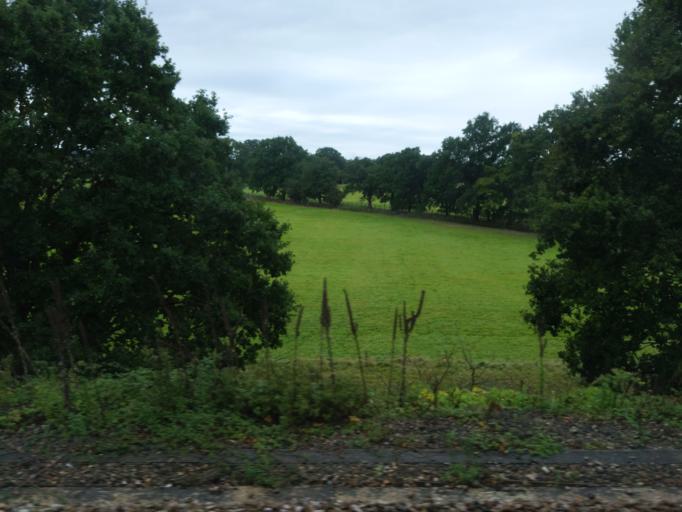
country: GB
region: England
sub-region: Kent
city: Tonbridge
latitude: 51.2059
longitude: 0.2489
